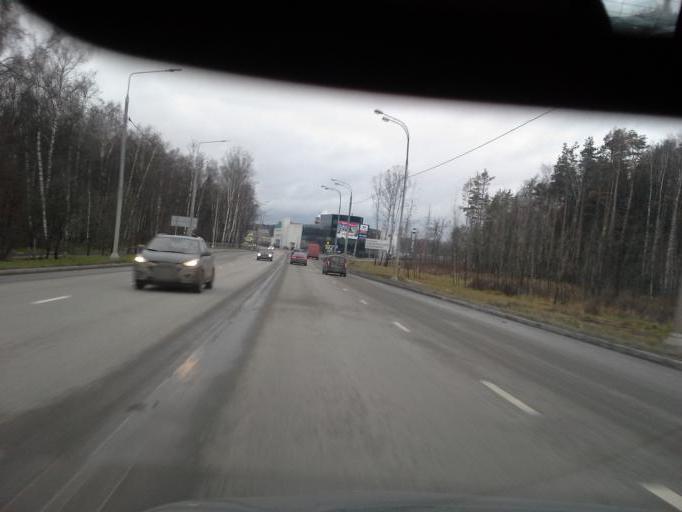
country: RU
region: Moskovskaya
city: Moskovskiy
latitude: 55.6117
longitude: 37.3499
